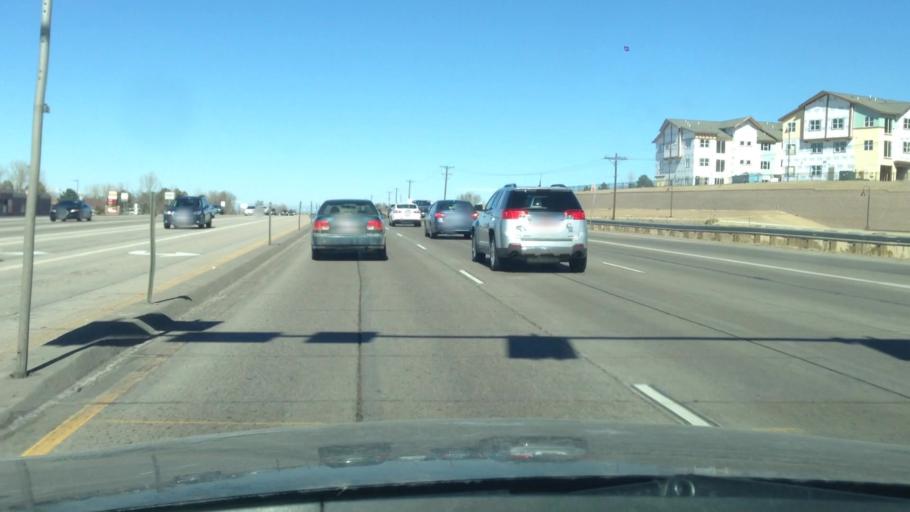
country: US
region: Colorado
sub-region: Douglas County
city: Stonegate
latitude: 39.5587
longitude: -104.7800
